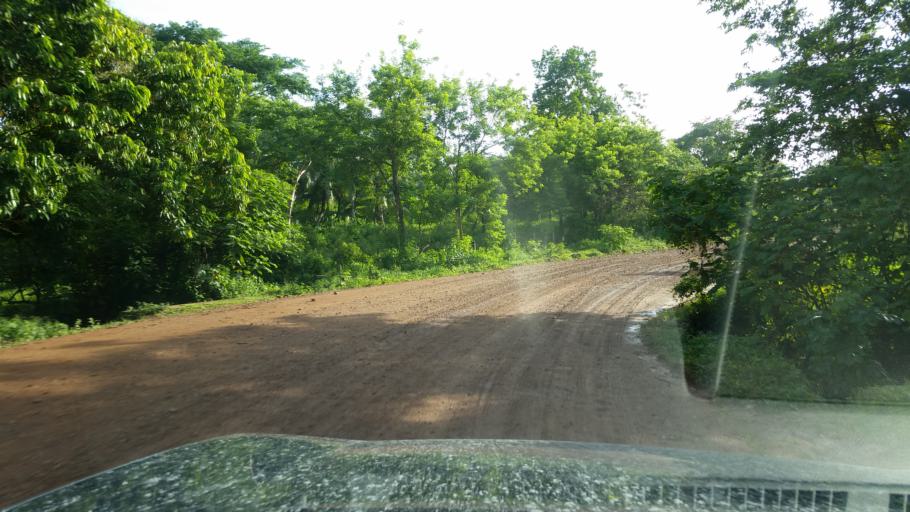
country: NI
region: Atlantico Norte (RAAN)
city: Puerto Cabezas
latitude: 14.0929
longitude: -83.8421
